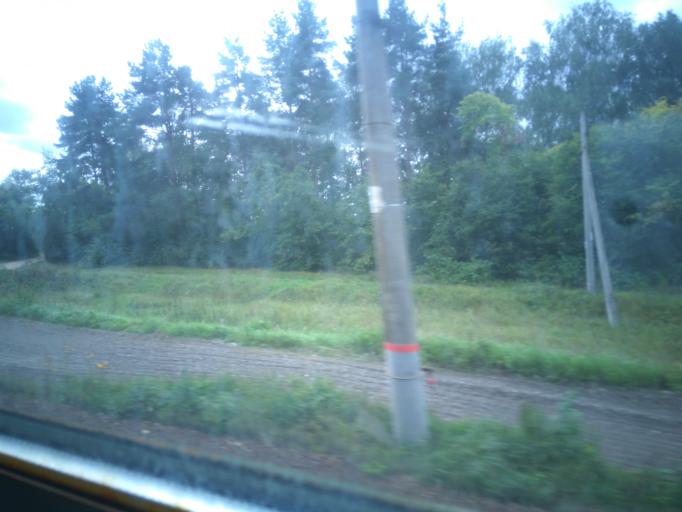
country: RU
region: Moskovskaya
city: Beloozerskiy
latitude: 55.4823
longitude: 38.4030
